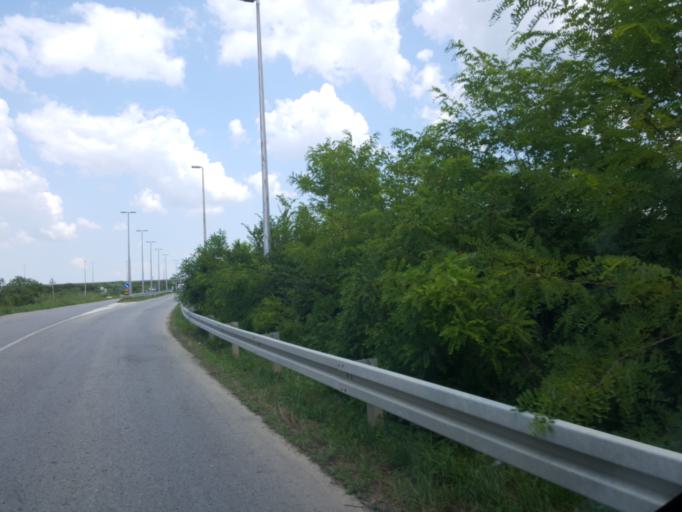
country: RS
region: Autonomna Pokrajina Vojvodina
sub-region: Sremski Okrug
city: Sid
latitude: 45.0438
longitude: 19.2137
